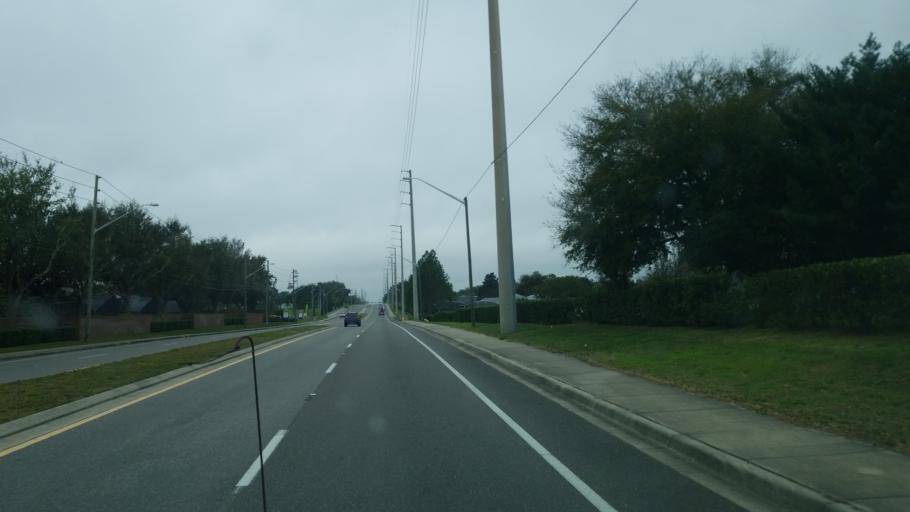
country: US
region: Florida
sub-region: Lake County
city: Four Corners
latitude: 28.2573
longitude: -81.6415
